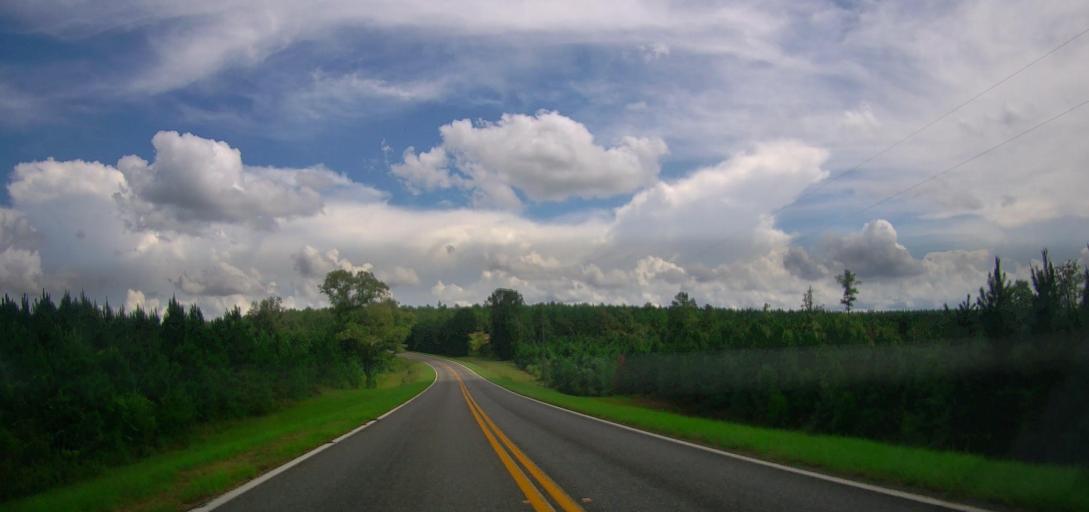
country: US
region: Georgia
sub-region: Taylor County
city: Butler
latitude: 32.4358
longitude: -84.1897
